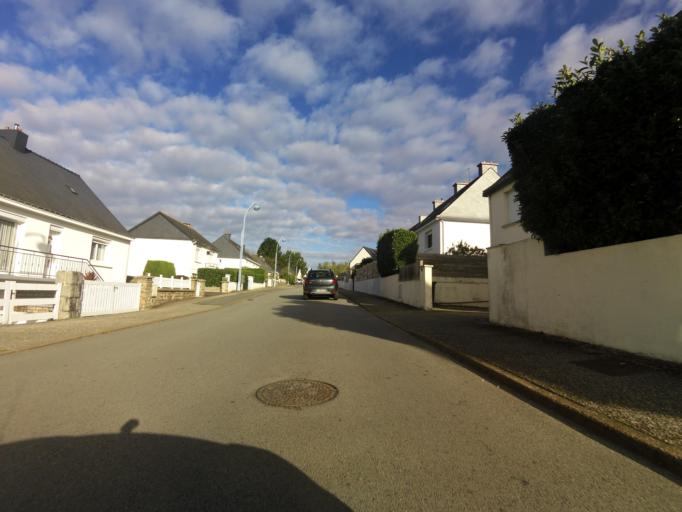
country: FR
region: Brittany
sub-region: Departement du Morbihan
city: Saint-Ave
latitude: 47.6859
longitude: -2.7379
